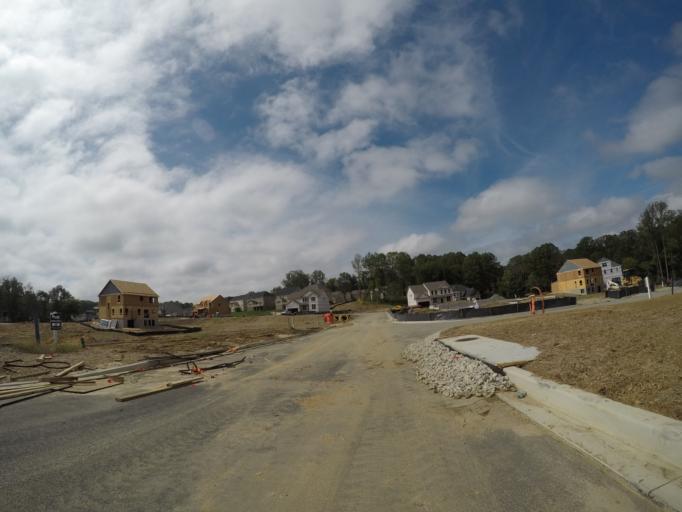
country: US
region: Maryland
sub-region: Howard County
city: Ellicott City
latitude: 39.3091
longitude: -76.8185
